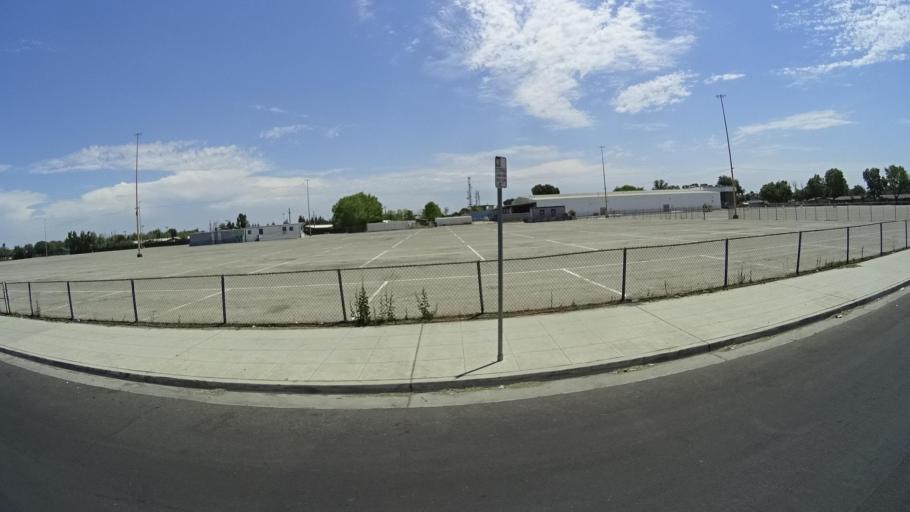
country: US
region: California
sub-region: Fresno County
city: Fresno
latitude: 36.7262
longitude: -119.7515
